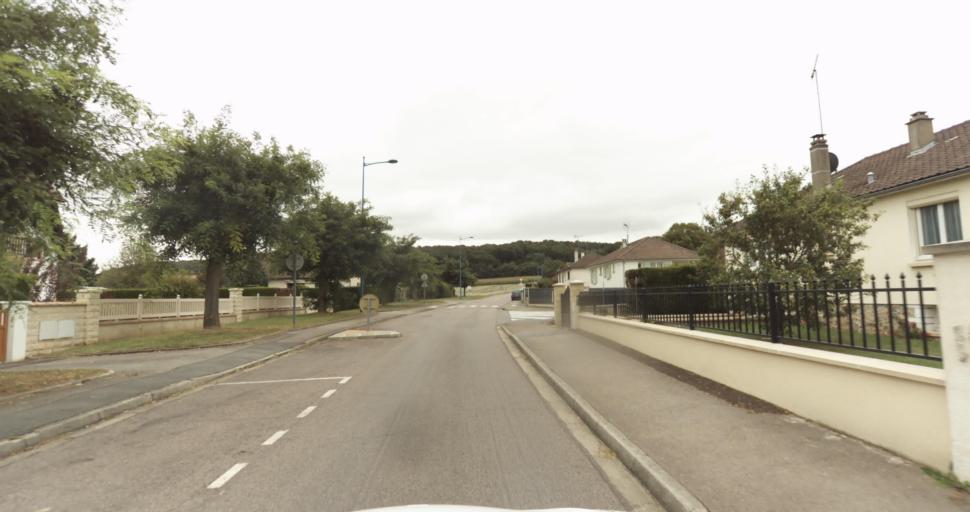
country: FR
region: Haute-Normandie
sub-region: Departement de l'Eure
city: Gravigny
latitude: 49.0465
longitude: 1.1676
